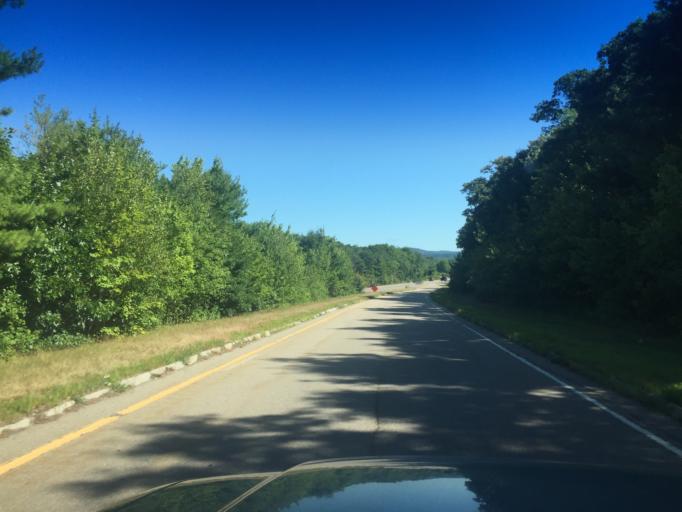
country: US
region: Massachusetts
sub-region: Norfolk County
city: Sharon
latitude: 42.1486
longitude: -71.1981
